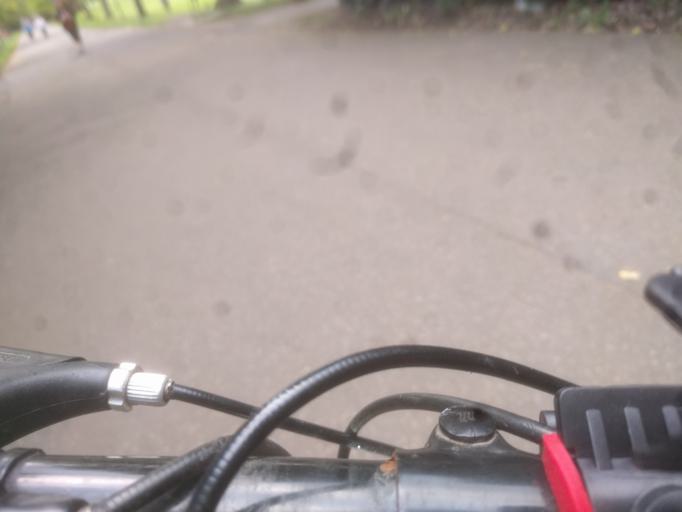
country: GB
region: Scotland
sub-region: Edinburgh
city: Edinburgh
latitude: 55.9627
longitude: -3.2206
